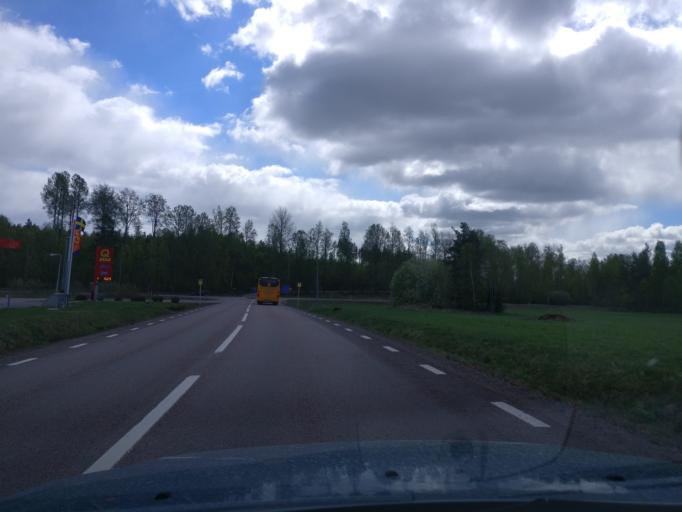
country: SE
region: Vaermland
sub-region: Karlstads Kommun
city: Molkom
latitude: 59.6045
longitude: 13.7392
